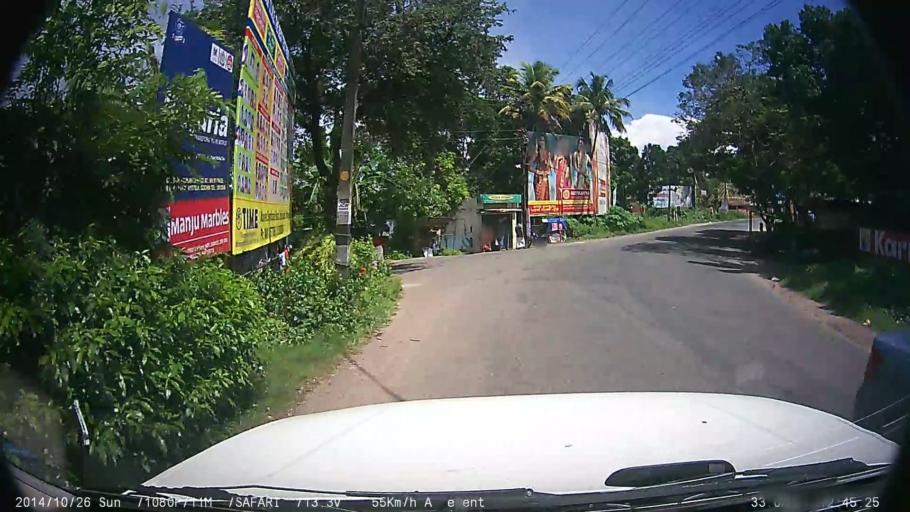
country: IN
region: Kerala
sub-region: Kottayam
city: Kottayam
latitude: 9.5281
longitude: 76.5184
